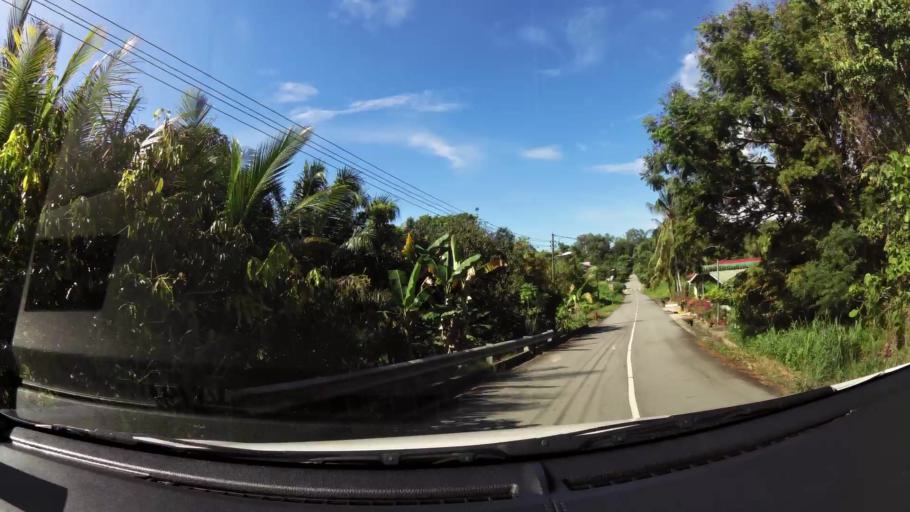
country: BN
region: Brunei and Muara
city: Bandar Seri Begawan
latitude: 4.9662
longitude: 114.9270
